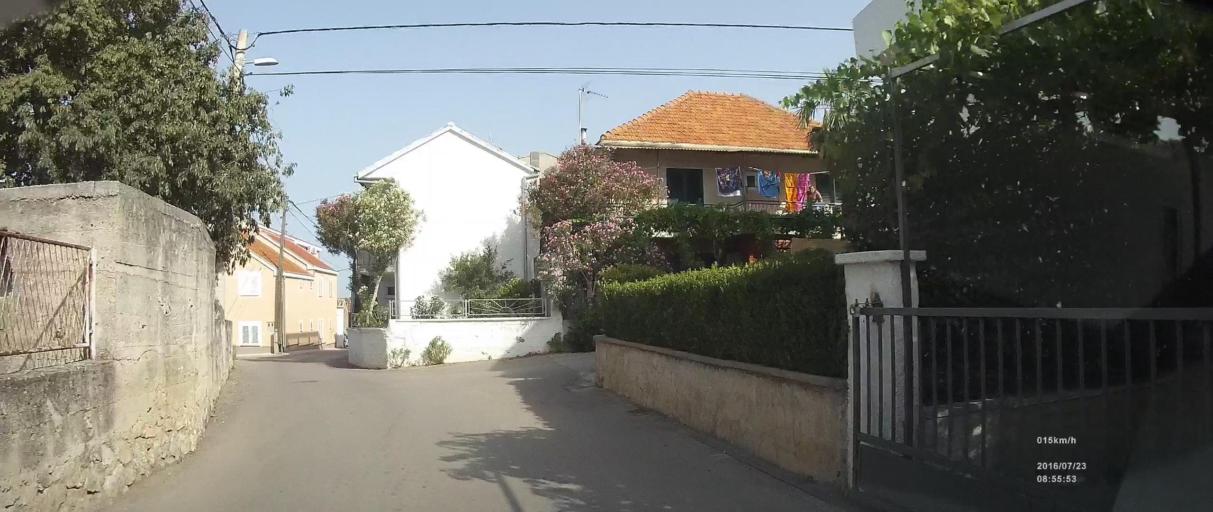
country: HR
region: Zadarska
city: Pakostane
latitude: 43.9091
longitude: 15.5101
